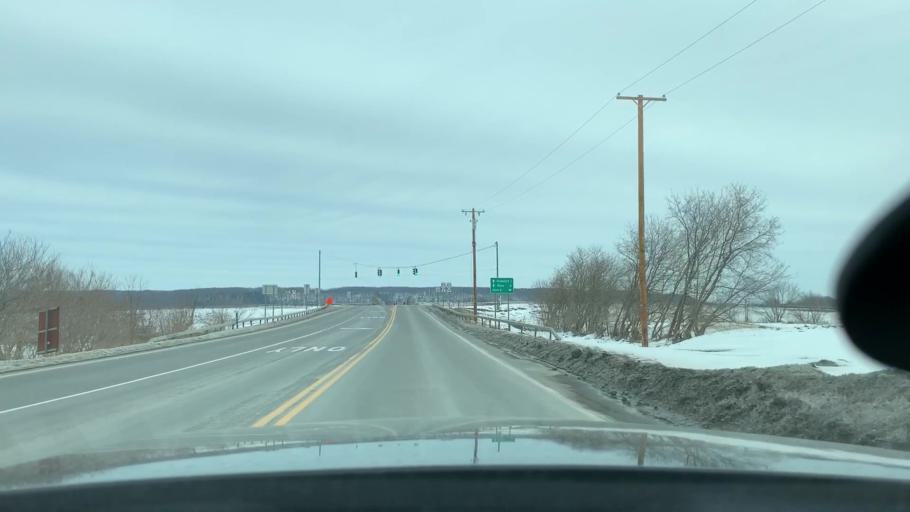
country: US
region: New York
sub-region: Herkimer County
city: Frankfort
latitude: 43.0394
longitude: -75.0879
